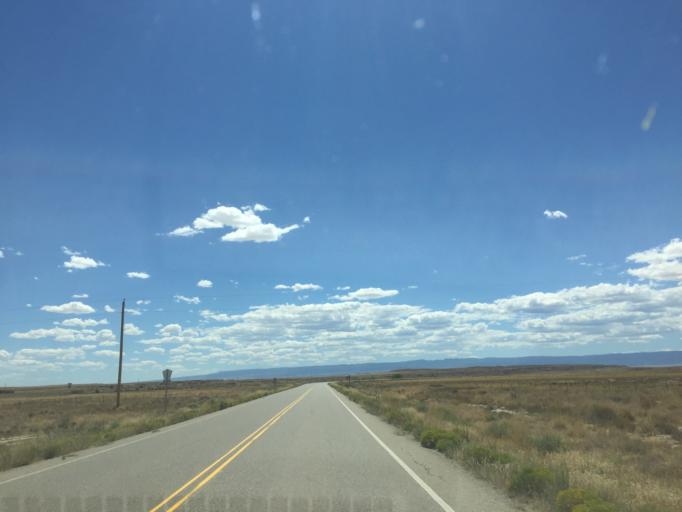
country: US
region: New Mexico
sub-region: San Juan County
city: Waterflow
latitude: 36.3756
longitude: -108.5009
